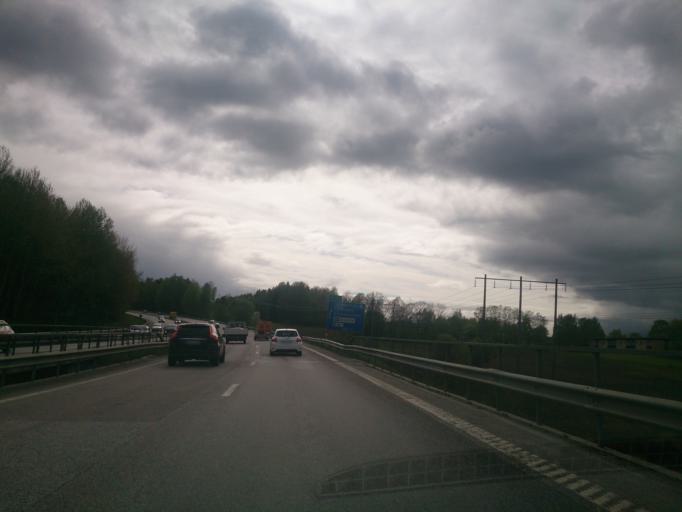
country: SE
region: Soedermanland
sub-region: Nykopings Kommun
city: Nykoping
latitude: 58.7690
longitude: 16.9991
